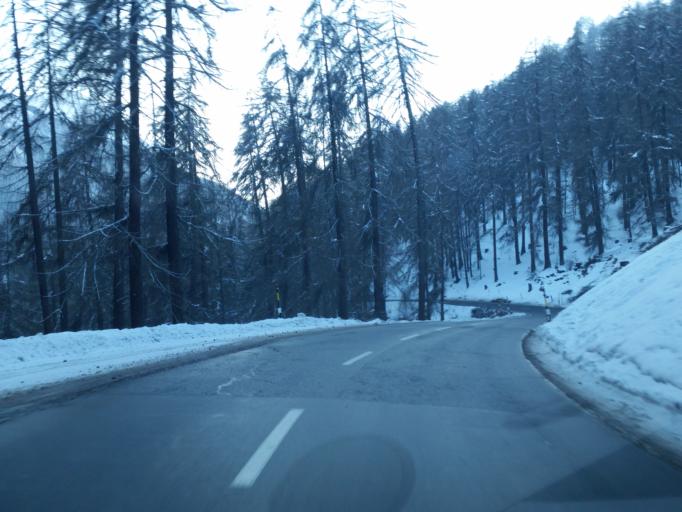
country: CH
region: Grisons
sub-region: Inn District
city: Zernez
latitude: 46.7739
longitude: 10.1755
